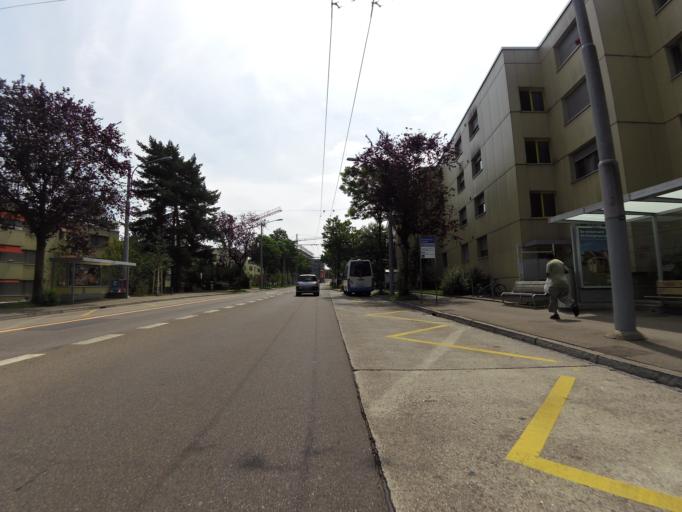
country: CH
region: Zurich
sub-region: Bezirk Zuerich
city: Zuerich (Kreis 3) / Friesenberg
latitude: 47.3623
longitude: 8.5048
